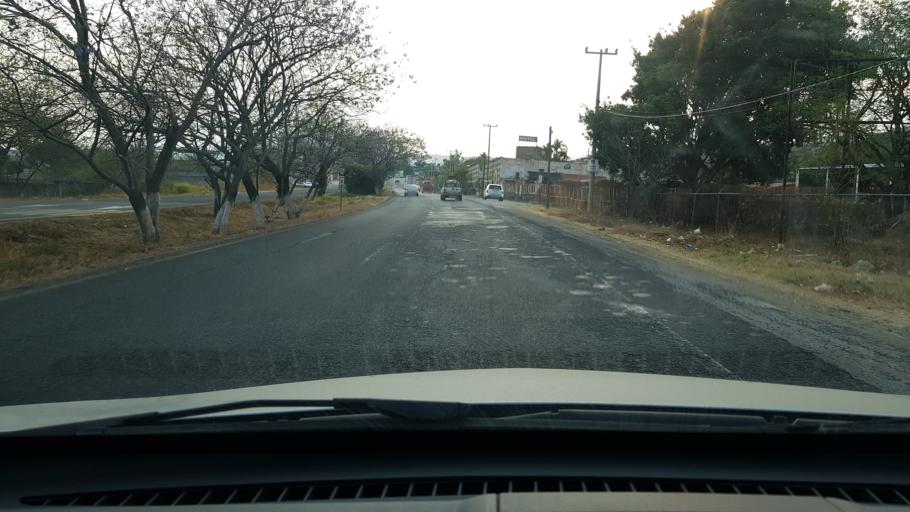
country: MX
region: Morelos
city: Yautepec
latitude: 18.8715
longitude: -99.0769
